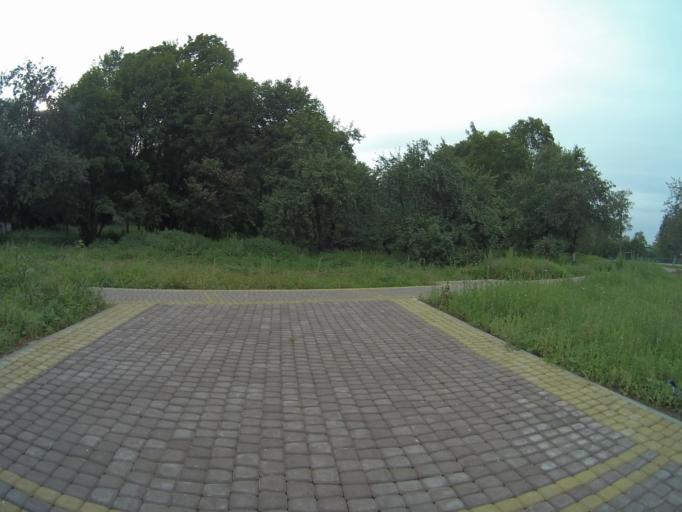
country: RU
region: Vladimir
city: Bogolyubovo
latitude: 56.1967
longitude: 40.5343
